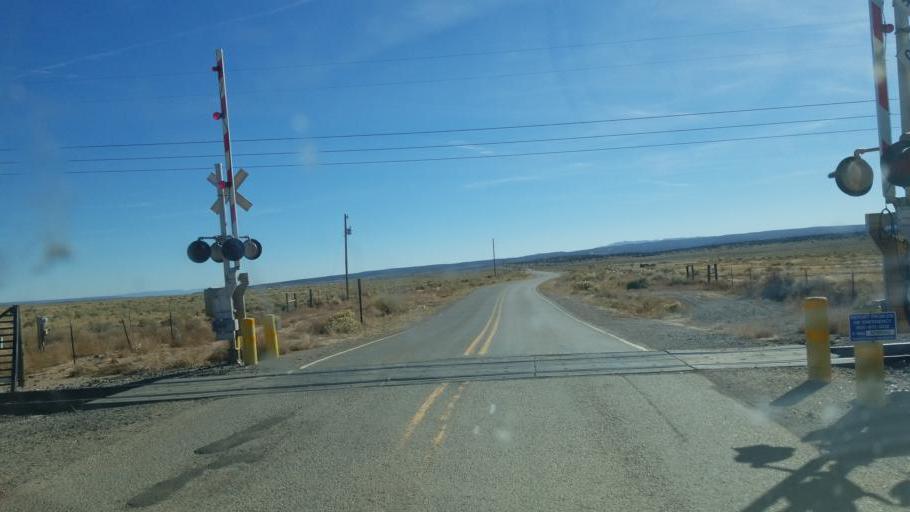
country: US
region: New Mexico
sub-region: McKinley County
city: Thoreau
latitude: 35.4210
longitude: -108.0522
